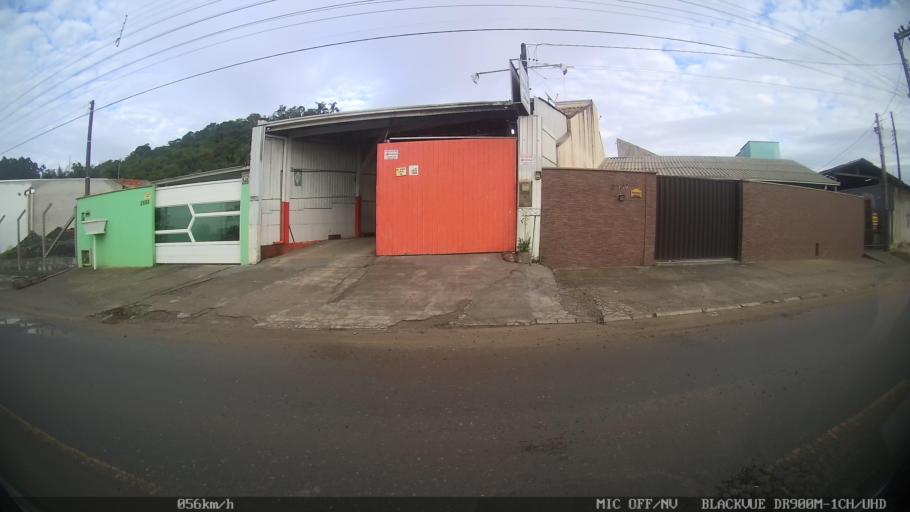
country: BR
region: Santa Catarina
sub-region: Barra Velha
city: Barra Velha
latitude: -26.6274
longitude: -48.7013
